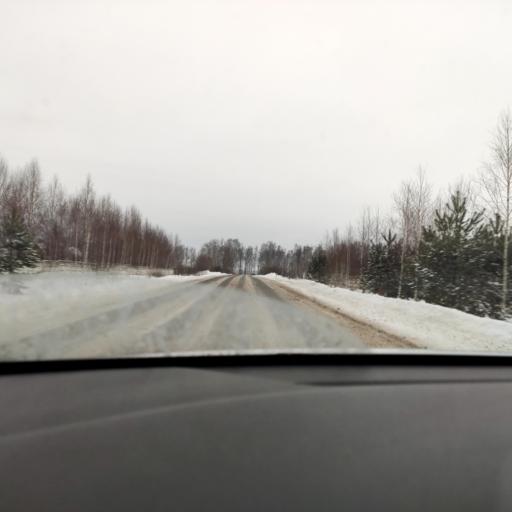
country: RU
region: Tatarstan
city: Osinovo
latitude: 55.8584
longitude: 48.8208
